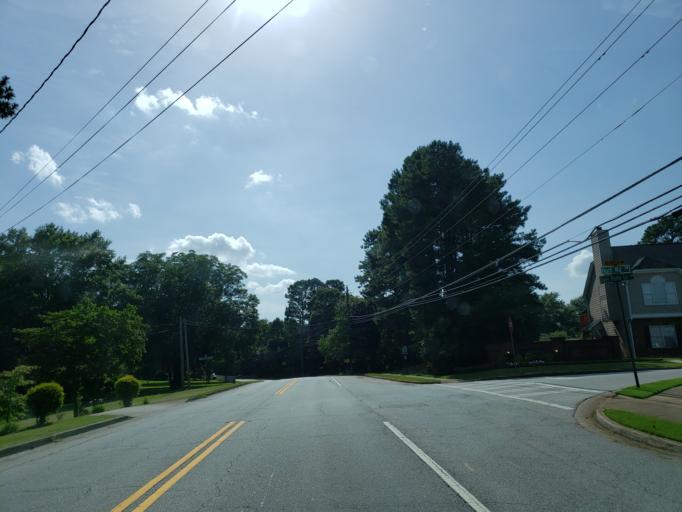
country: US
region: Georgia
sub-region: Cobb County
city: Mableton
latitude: 33.8644
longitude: -84.5859
